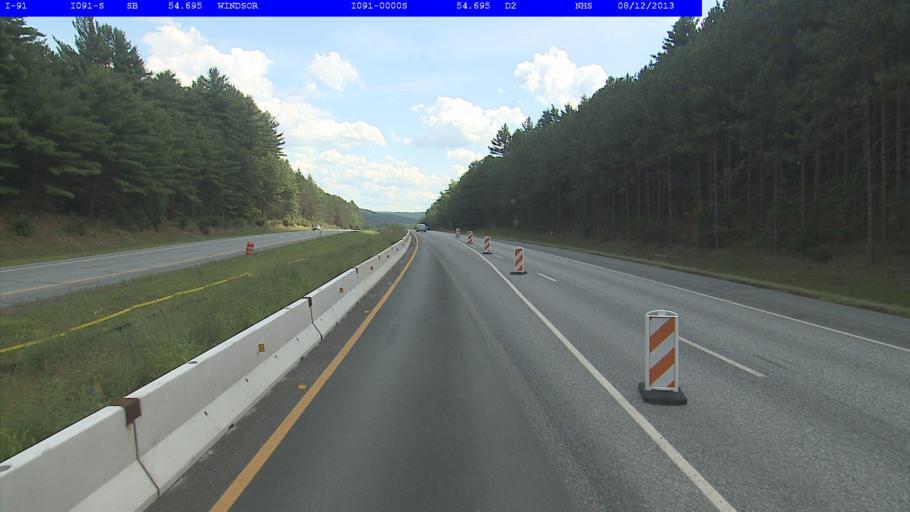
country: US
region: Vermont
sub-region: Windsor County
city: Windsor
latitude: 43.4474
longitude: -72.4064
